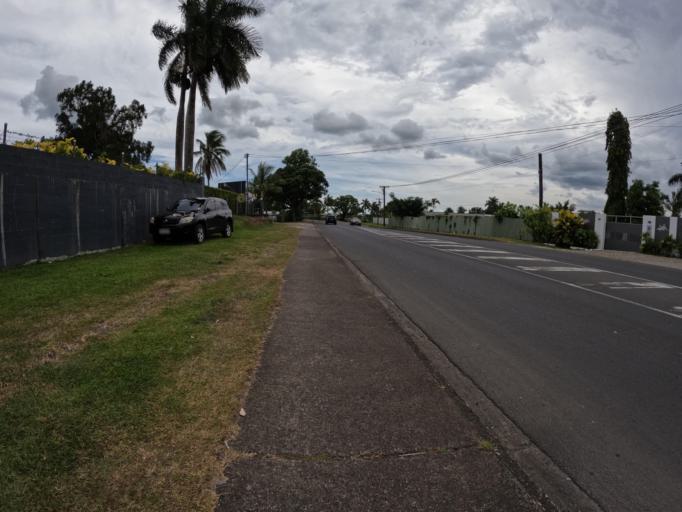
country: FJ
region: Central
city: Suva
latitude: -18.1152
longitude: 178.4383
